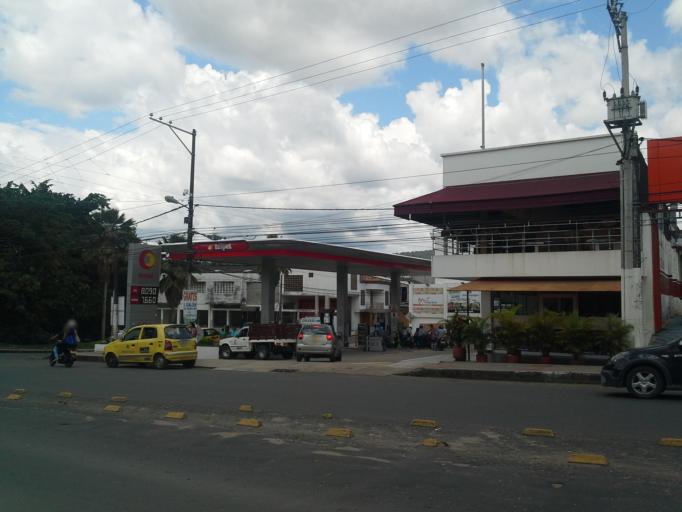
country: CO
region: Caqueta
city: Florencia
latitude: 1.6125
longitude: -75.6117
